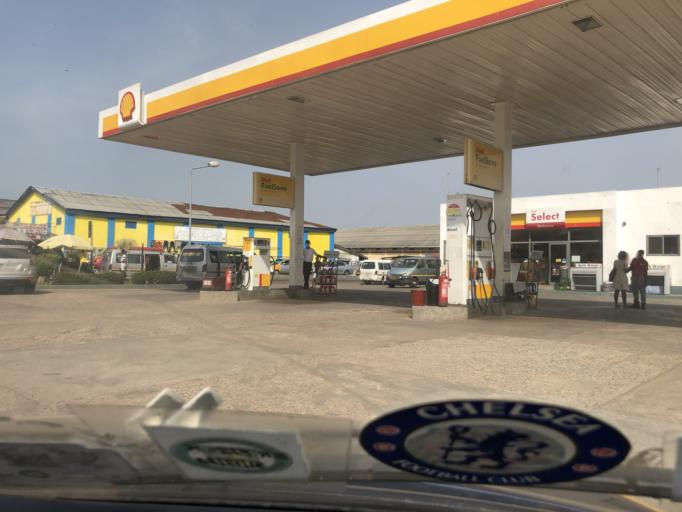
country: GH
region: Eastern
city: Koforidua
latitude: 6.0947
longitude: -0.2600
